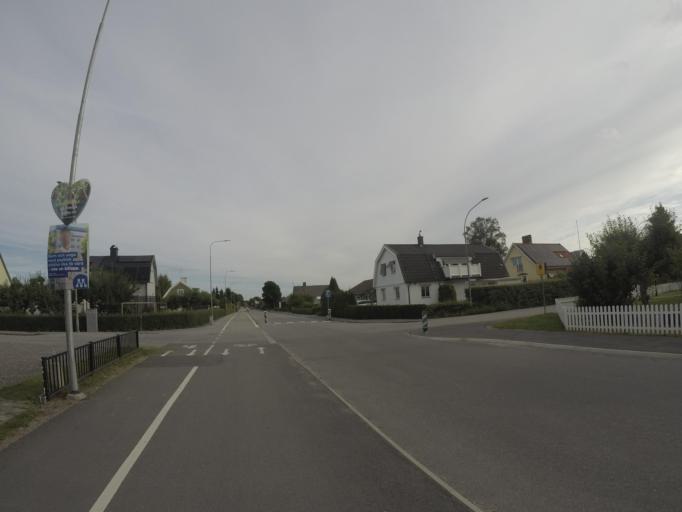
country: SE
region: OErebro
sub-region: Orebro Kommun
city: Orebro
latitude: 59.2574
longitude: 15.2486
